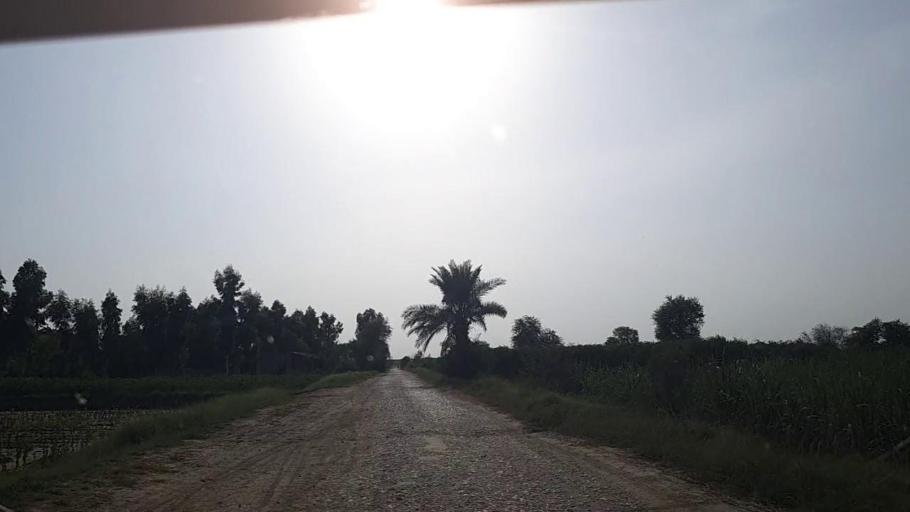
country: PK
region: Sindh
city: Ghotki
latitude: 28.0167
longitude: 69.2918
